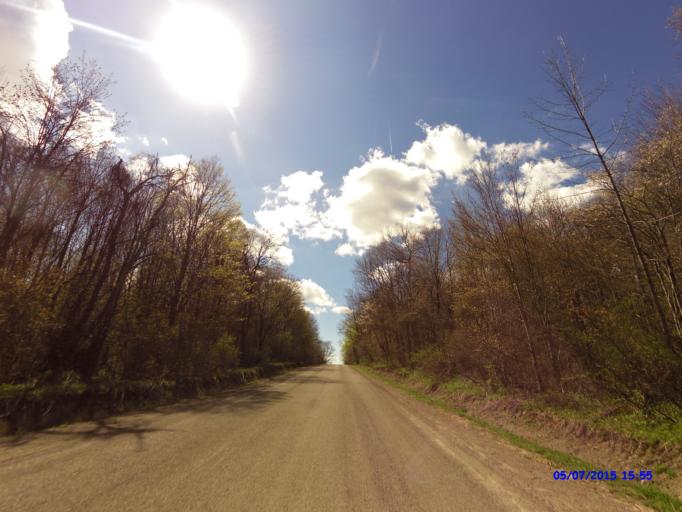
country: US
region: New York
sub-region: Cattaraugus County
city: Franklinville
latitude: 42.3148
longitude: -78.5530
